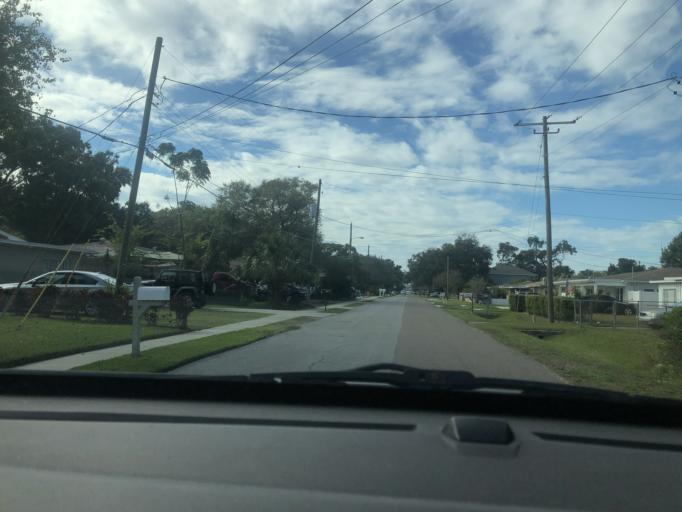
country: US
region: Florida
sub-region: Hillsborough County
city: Tampa
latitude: 27.9493
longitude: -82.5079
